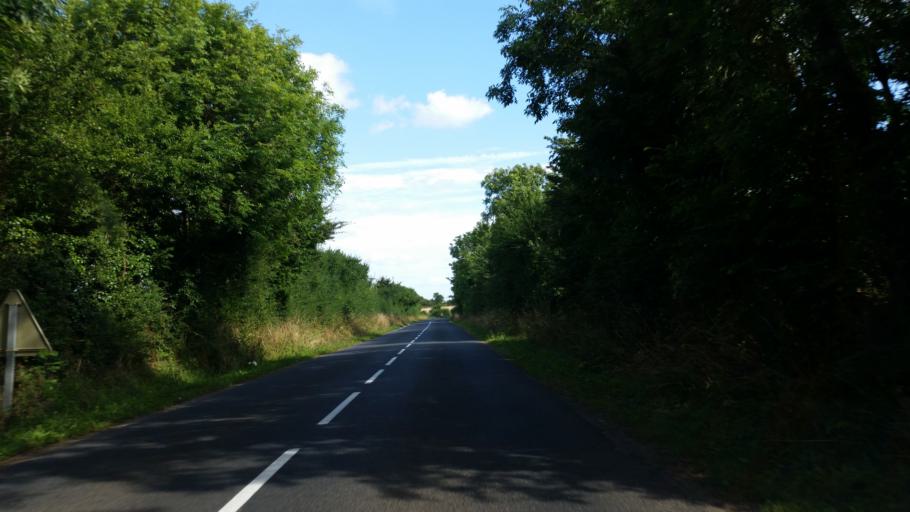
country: FR
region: Lower Normandy
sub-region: Departement de la Manche
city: Sainte-Mere-Eglise
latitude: 49.4532
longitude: -1.2673
